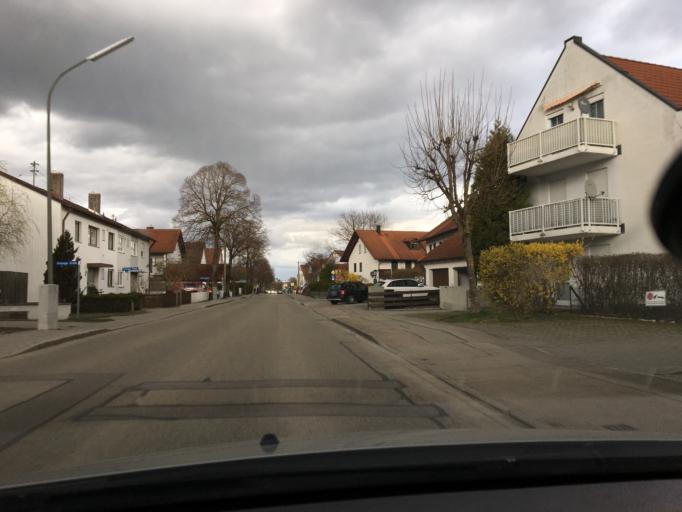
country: DE
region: Bavaria
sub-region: Upper Bavaria
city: Hallbergmoos
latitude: 48.3119
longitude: 11.7425
